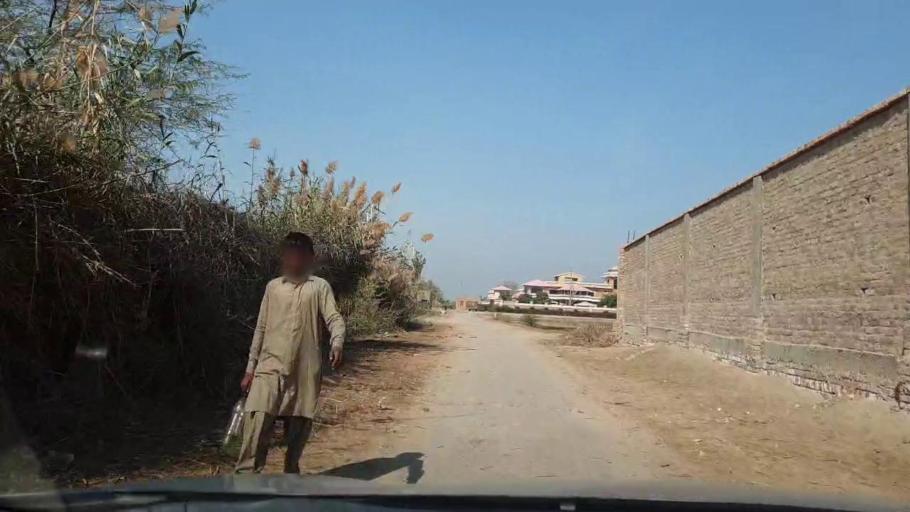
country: PK
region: Sindh
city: Berani
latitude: 25.6884
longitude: 68.7545
